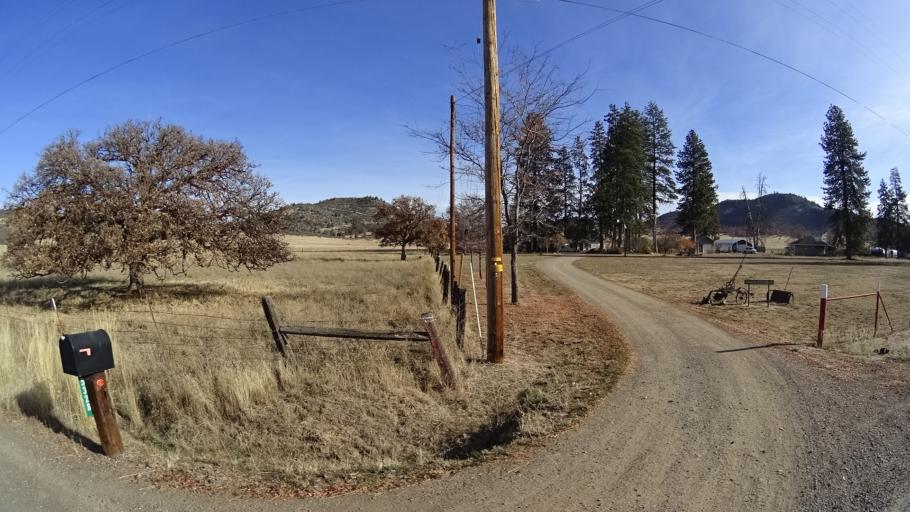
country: US
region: California
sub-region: Siskiyou County
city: Yreka
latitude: 41.6685
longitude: -122.6084
